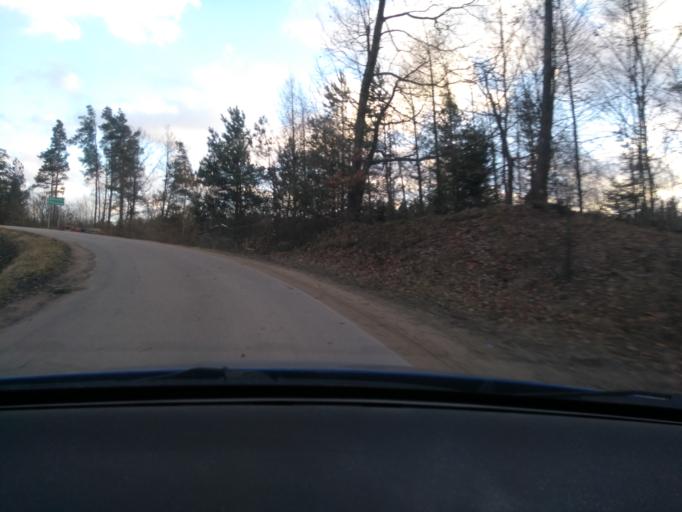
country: PL
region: Pomeranian Voivodeship
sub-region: Powiat kartuski
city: Przodkowo
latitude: 54.4141
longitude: 18.2503
